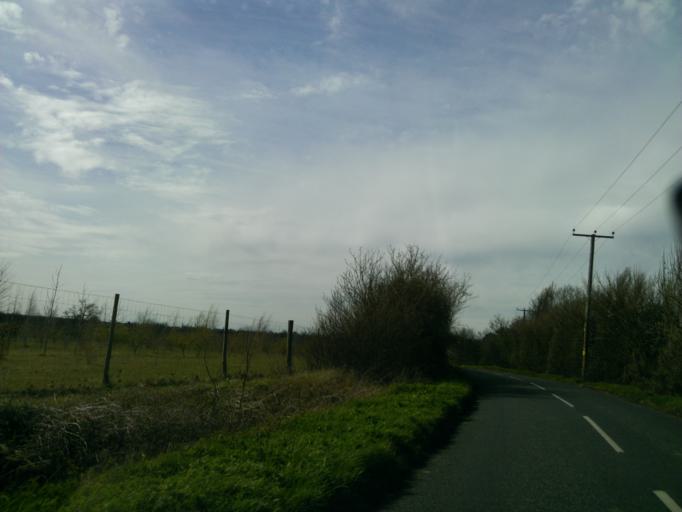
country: GB
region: England
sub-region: Essex
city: Coggeshall
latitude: 51.8426
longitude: 0.6591
